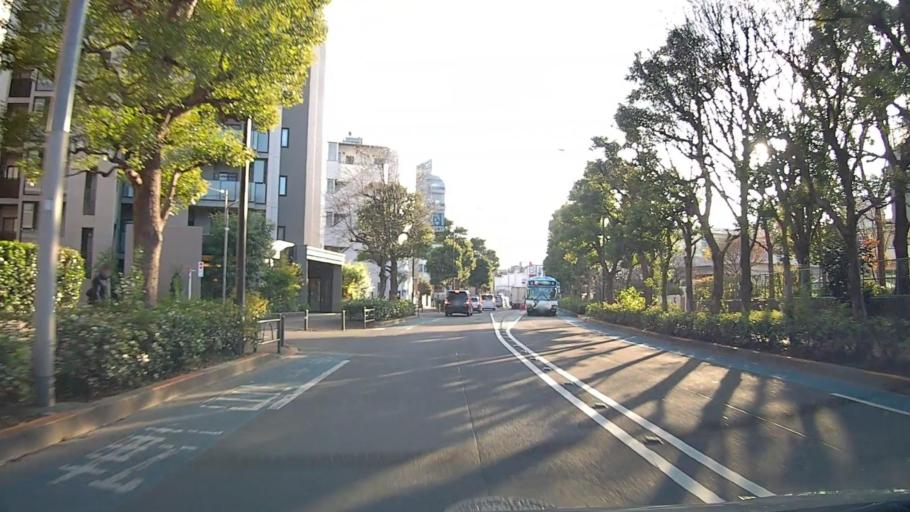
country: JP
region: Saitama
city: Wako
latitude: 35.7550
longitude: 139.6322
